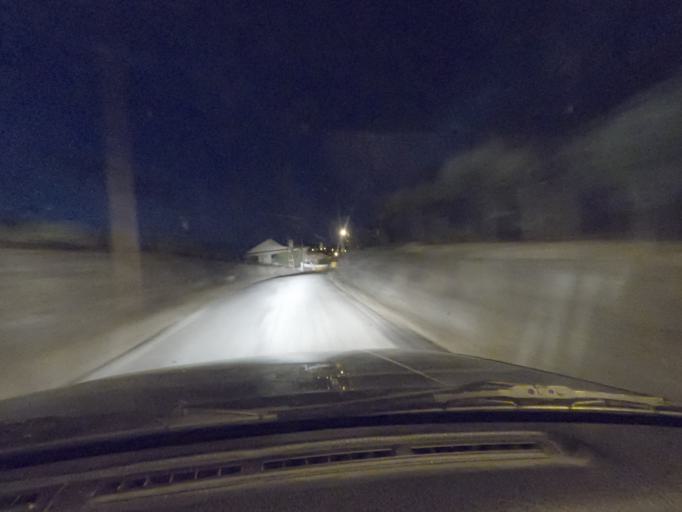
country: PT
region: Vila Real
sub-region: Santa Marta de Penaguiao
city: Santa Marta de Penaguiao
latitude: 41.2093
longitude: -7.8425
